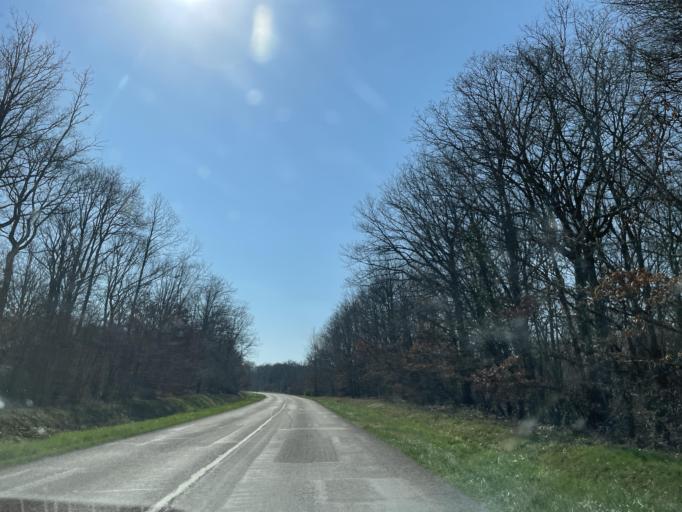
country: FR
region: Bourgogne
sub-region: Departement de la Cote-d'Or
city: Semur-en-Auxois
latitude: 47.4684
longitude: 4.3473
